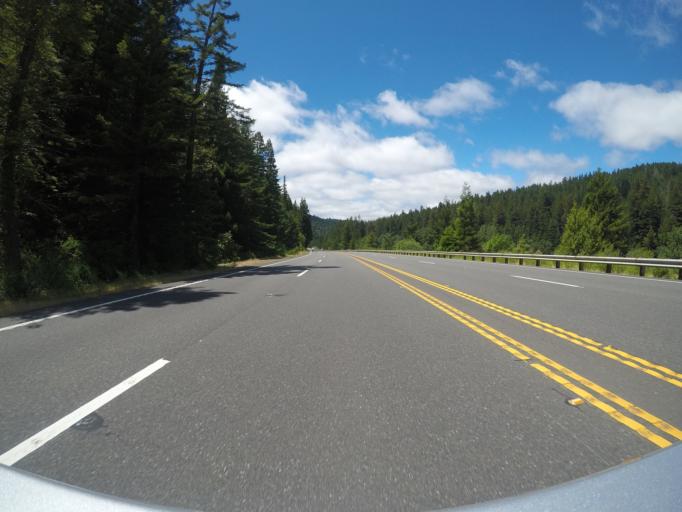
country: US
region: California
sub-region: Humboldt County
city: Redway
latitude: 40.2549
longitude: -123.8350
